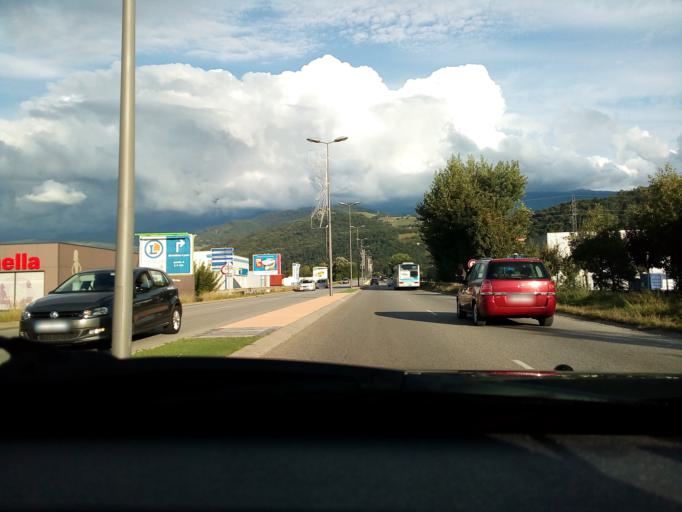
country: FR
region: Rhone-Alpes
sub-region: Departement de l'Isere
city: Saint-Martin-d'Heres
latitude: 45.1839
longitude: 5.7701
